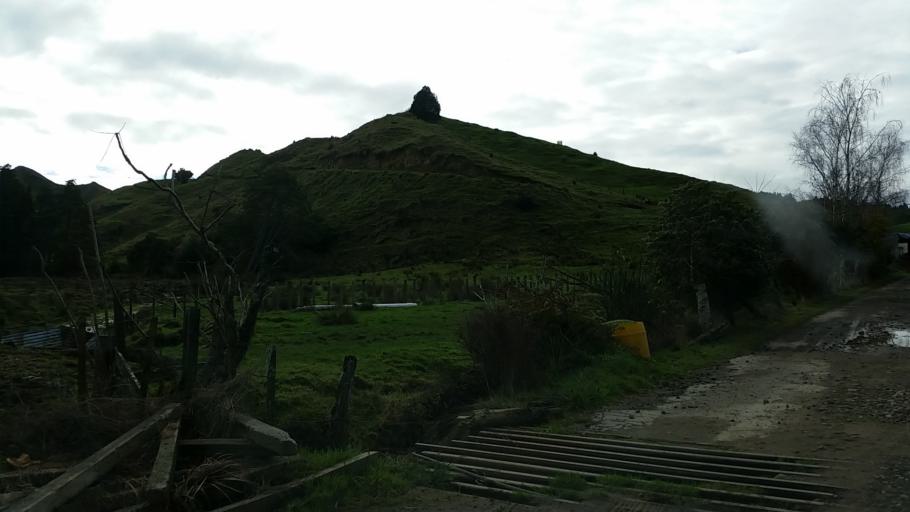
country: NZ
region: Taranaki
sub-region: South Taranaki District
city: Eltham
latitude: -39.2321
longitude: 174.5197
